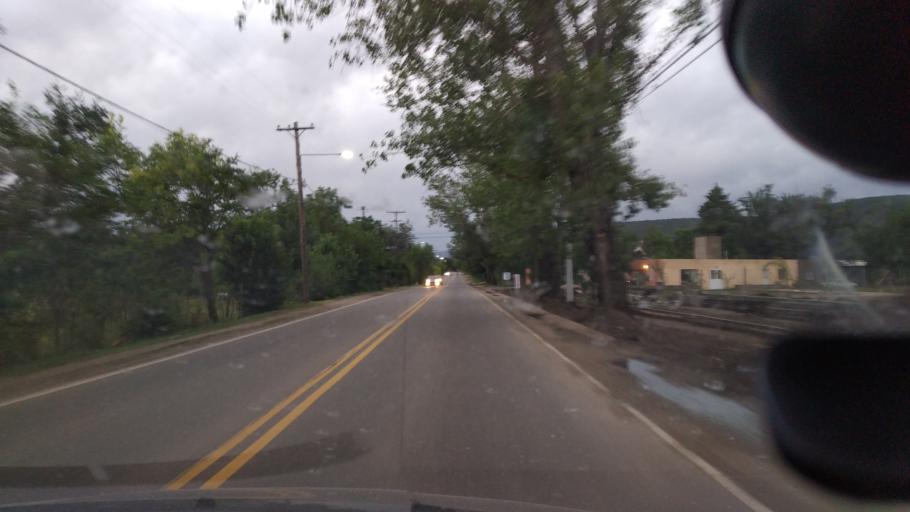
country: AR
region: Cordoba
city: Villa Las Rosas
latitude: -31.9164
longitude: -65.0373
